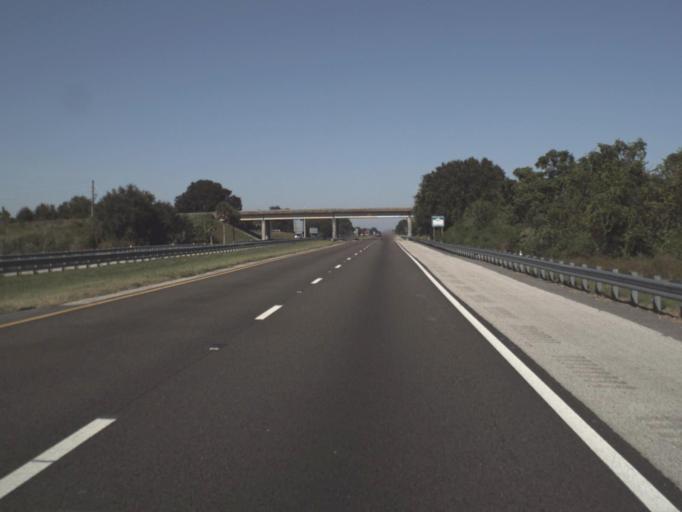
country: US
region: Florida
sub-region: Lake County
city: Yalaha
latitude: 28.6830
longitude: -81.8623
